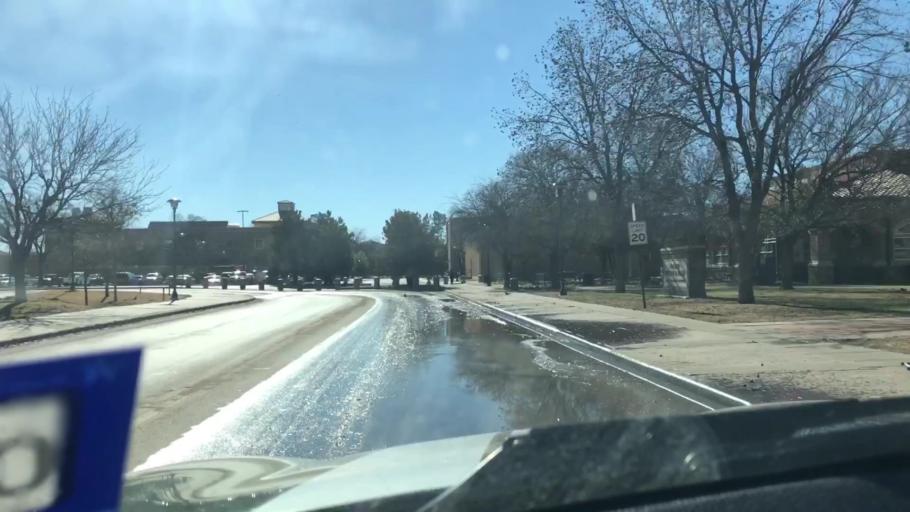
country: US
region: Texas
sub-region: Lubbock County
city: Lubbock
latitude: 33.5895
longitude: -101.8743
